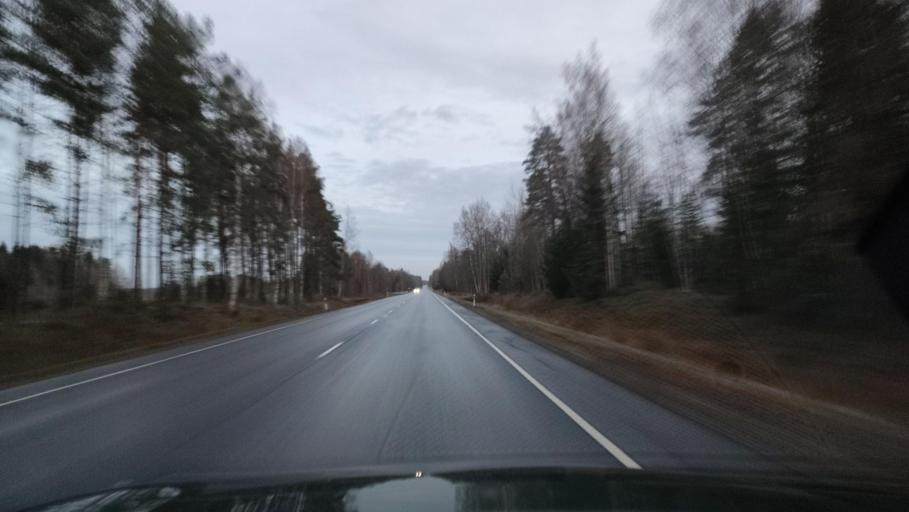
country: FI
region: Ostrobothnia
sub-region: Vaasa
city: Ristinummi
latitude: 62.9968
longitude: 21.7652
